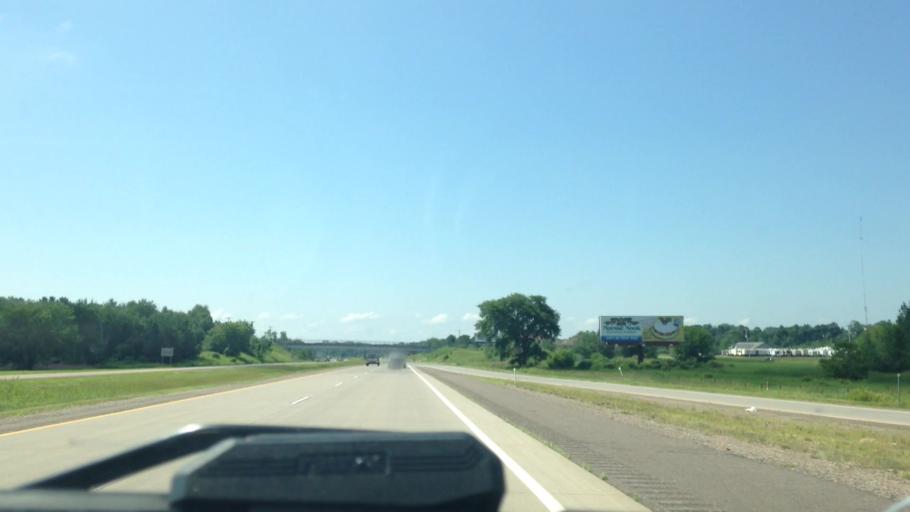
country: US
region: Wisconsin
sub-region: Barron County
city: Rice Lake
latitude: 45.5068
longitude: -91.7626
